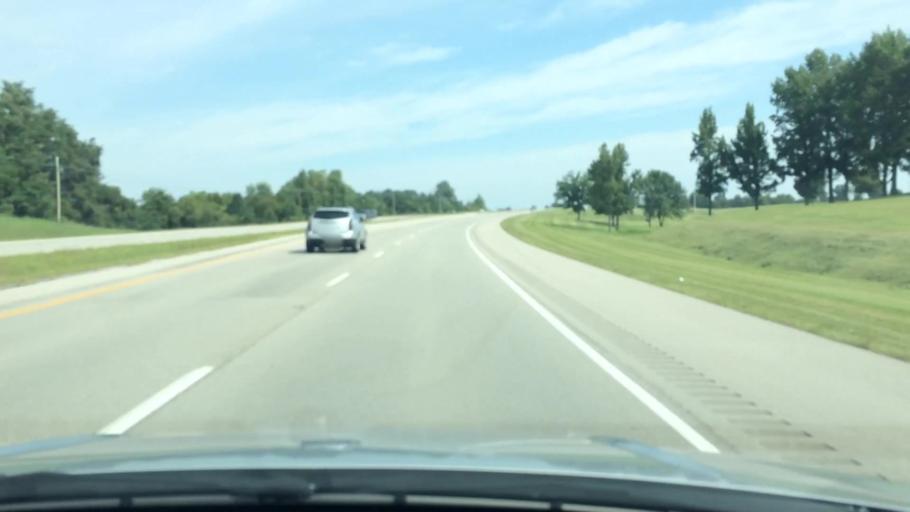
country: US
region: Kentucky
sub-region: Anderson County
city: Lawrenceburg
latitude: 38.1017
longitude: -84.9182
